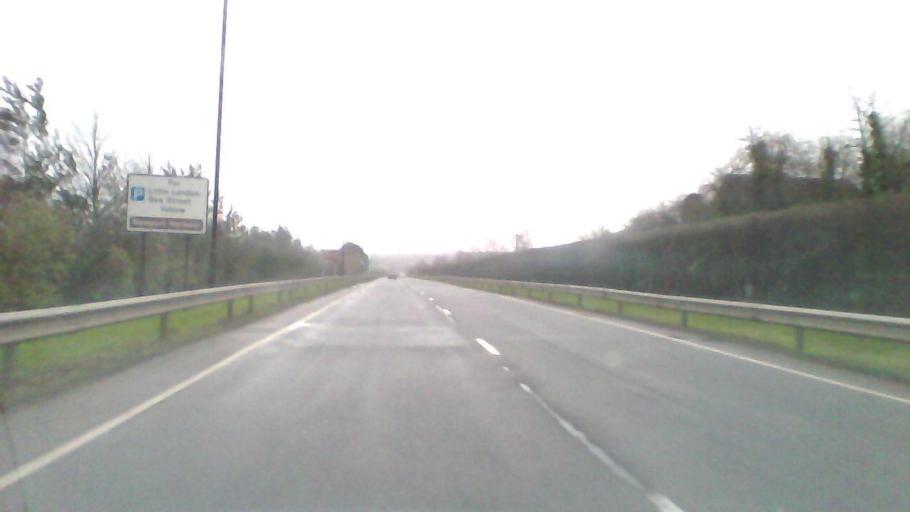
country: GB
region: England
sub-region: Isle of Wight
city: Newport
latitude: 50.7068
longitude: -1.2988
